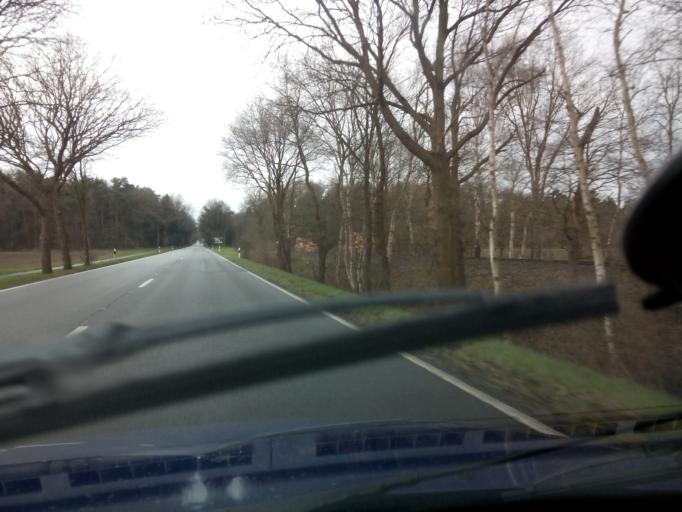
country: DE
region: Lower Saxony
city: Herzlake
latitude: 52.7063
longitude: 7.6311
